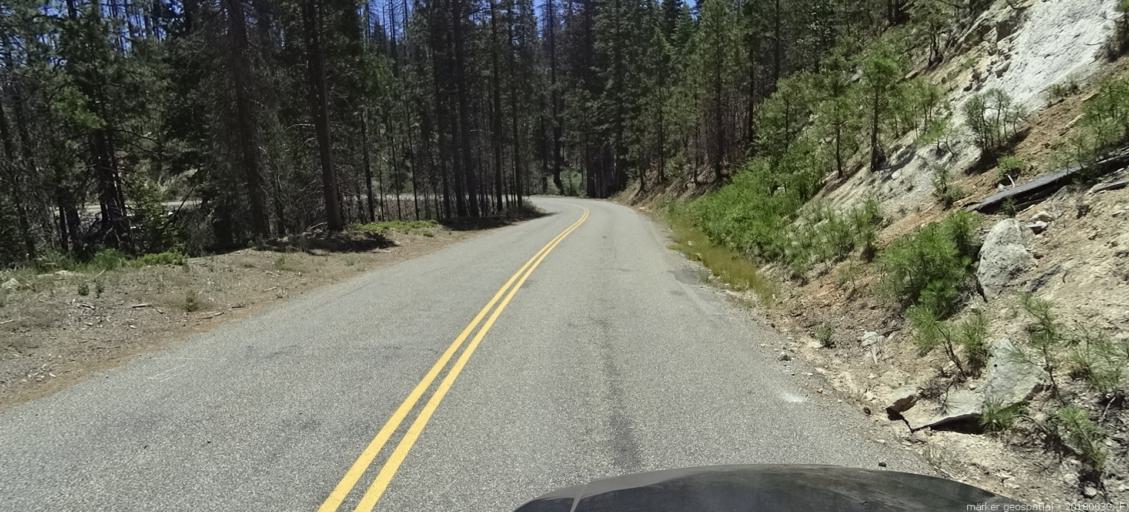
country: US
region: California
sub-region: Fresno County
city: Auberry
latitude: 37.3212
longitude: -119.3630
